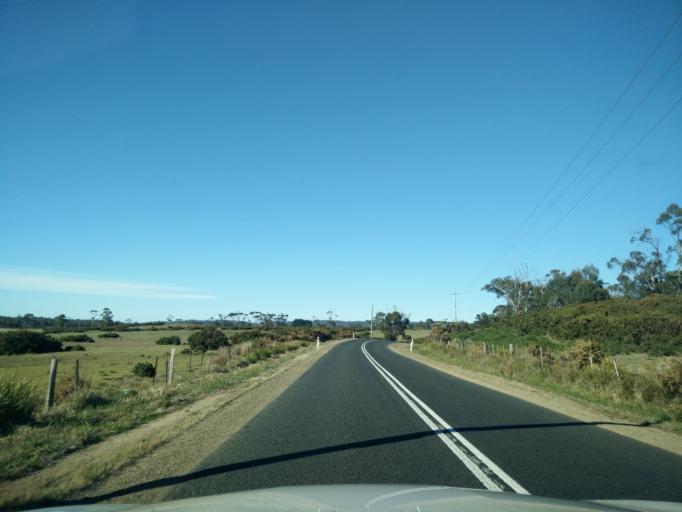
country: AU
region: Tasmania
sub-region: Break O'Day
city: St Helens
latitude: -41.9257
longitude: 148.2363
